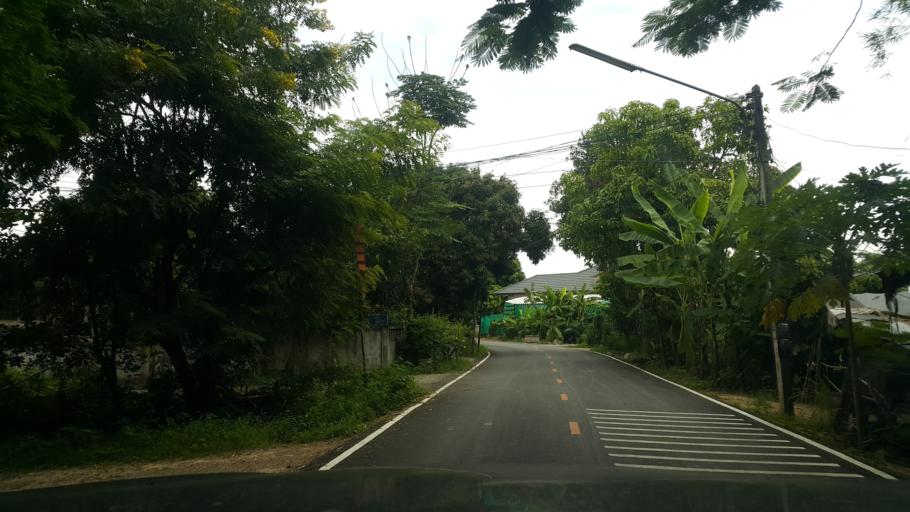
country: TH
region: Lamphun
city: Ban Thi
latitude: 18.6625
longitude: 99.1541
